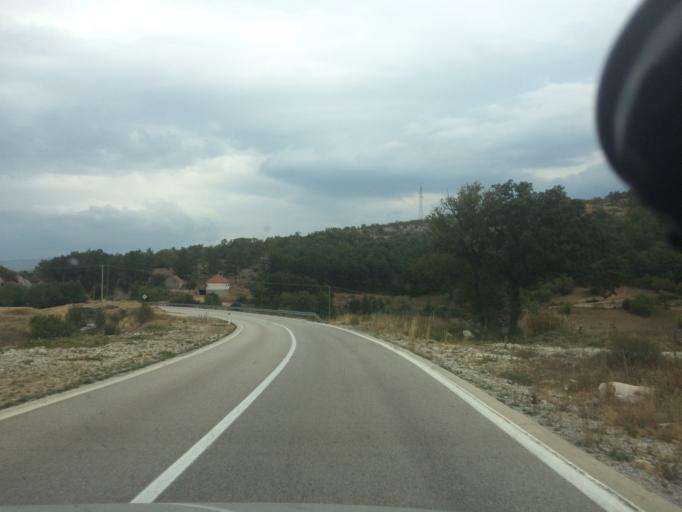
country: ME
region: Kotor
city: Risan
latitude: 42.7272
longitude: 18.6063
